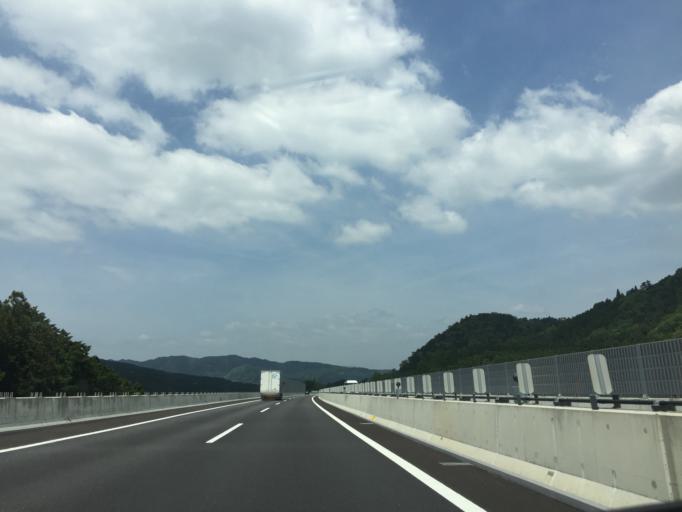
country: JP
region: Aichi
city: Shinshiro
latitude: 34.8932
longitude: 137.6328
